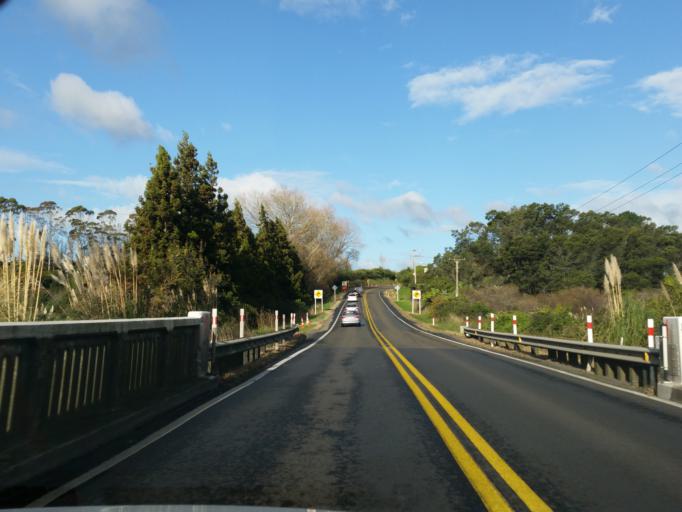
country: NZ
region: Bay of Plenty
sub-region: Western Bay of Plenty District
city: Katikati
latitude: -37.6341
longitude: 175.9597
